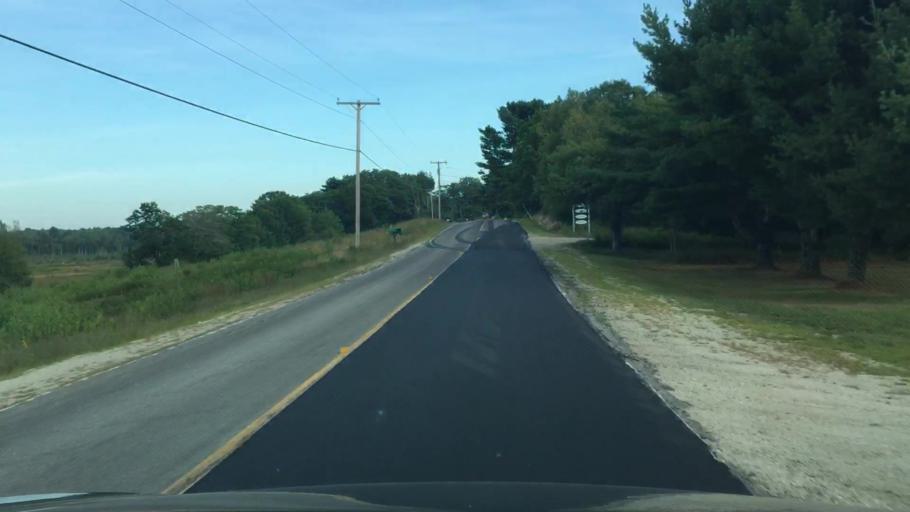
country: US
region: Maine
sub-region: Hancock County
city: Surry
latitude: 44.5149
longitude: -68.6030
